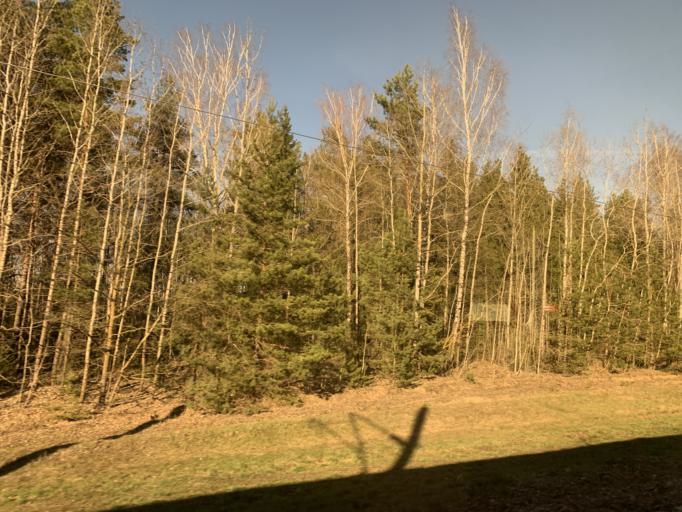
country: BY
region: Grodnenskaya
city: Smarhon'
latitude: 54.4367
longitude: 26.5133
